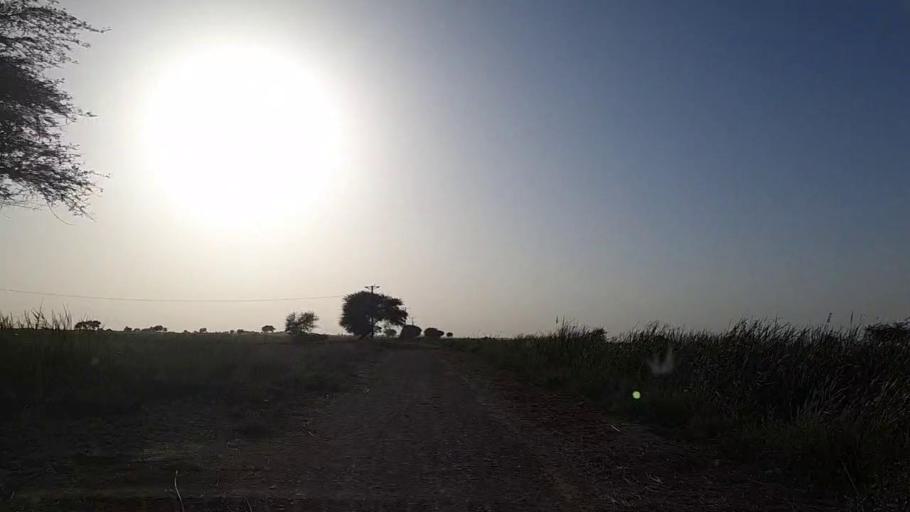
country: PK
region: Sindh
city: Jati
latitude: 24.4222
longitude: 68.2895
